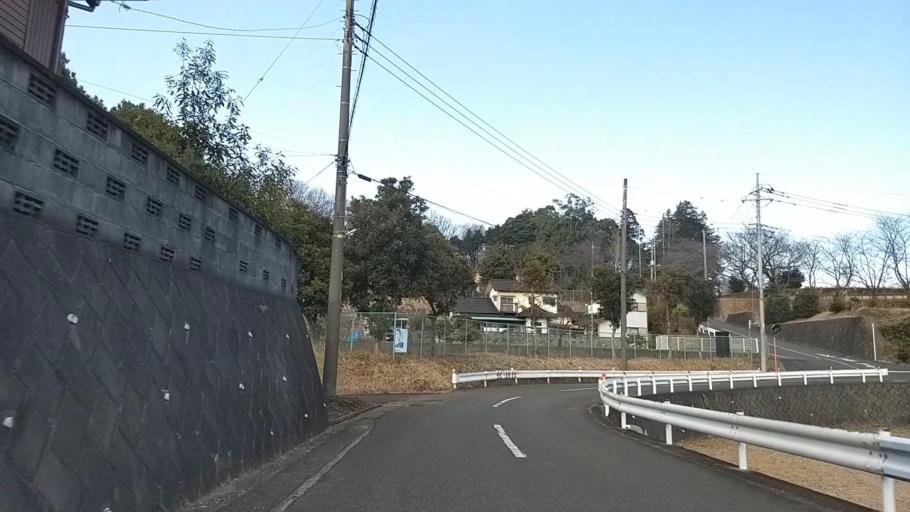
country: JP
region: Kanagawa
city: Isehara
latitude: 35.4284
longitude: 139.3146
